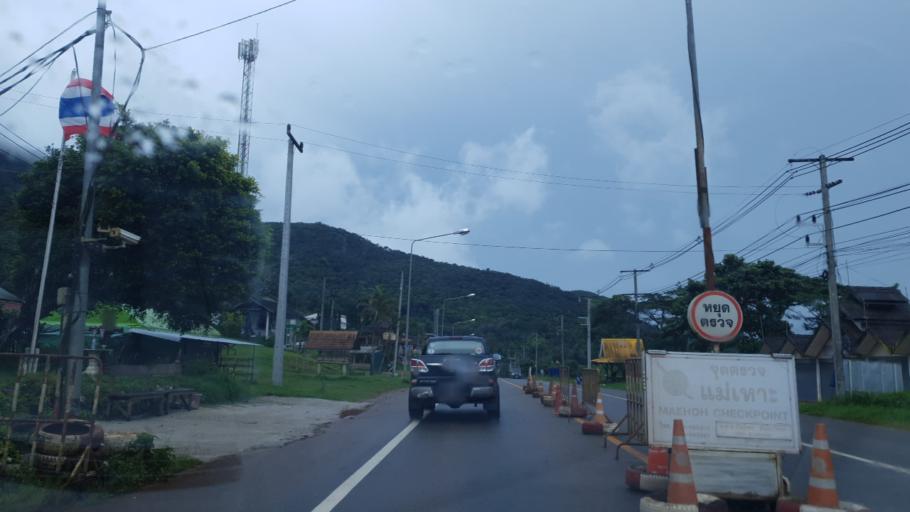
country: TH
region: Mae Hong Son
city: Ban Huai I Huak
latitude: 18.1541
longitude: 98.0687
